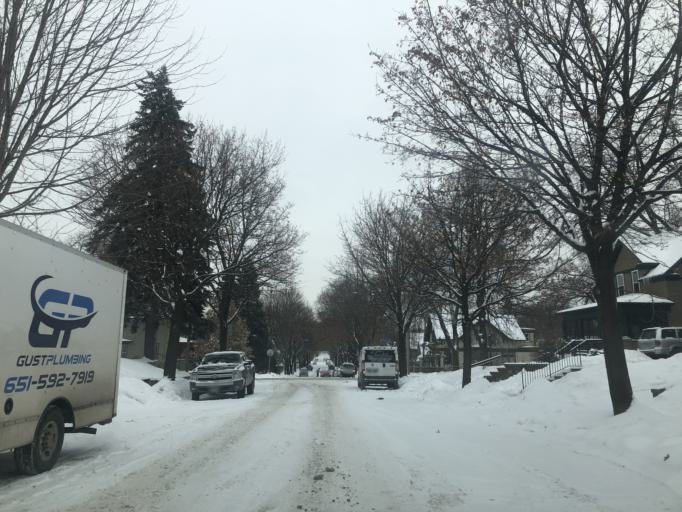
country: US
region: Minnesota
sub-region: Hennepin County
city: Richfield
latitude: 44.9274
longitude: -93.2818
